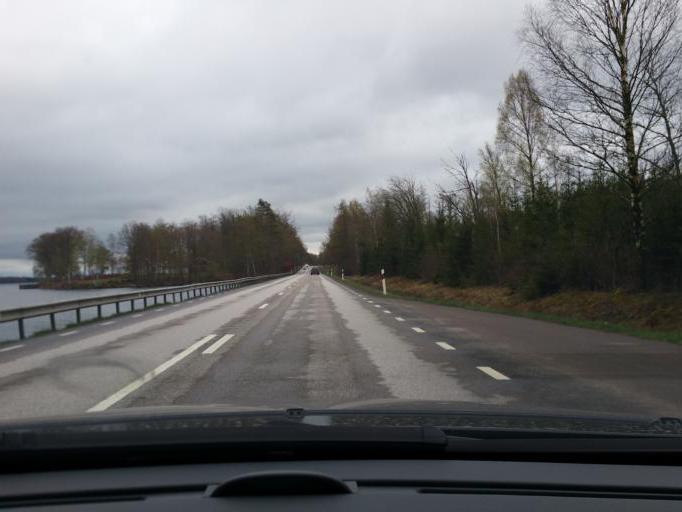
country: SE
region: Kronoberg
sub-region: Alvesta Kommun
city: Moheda
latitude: 56.9825
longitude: 14.6979
